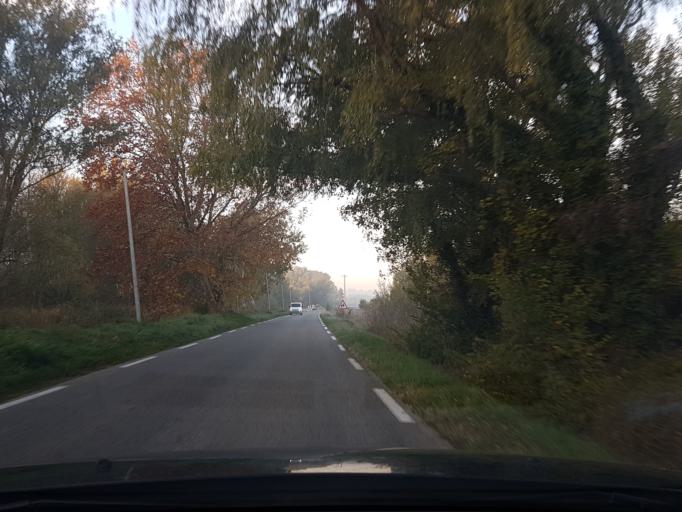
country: FR
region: Provence-Alpes-Cote d'Azur
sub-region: Departement du Vaucluse
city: Bedarrides
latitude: 44.0316
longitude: 4.9237
